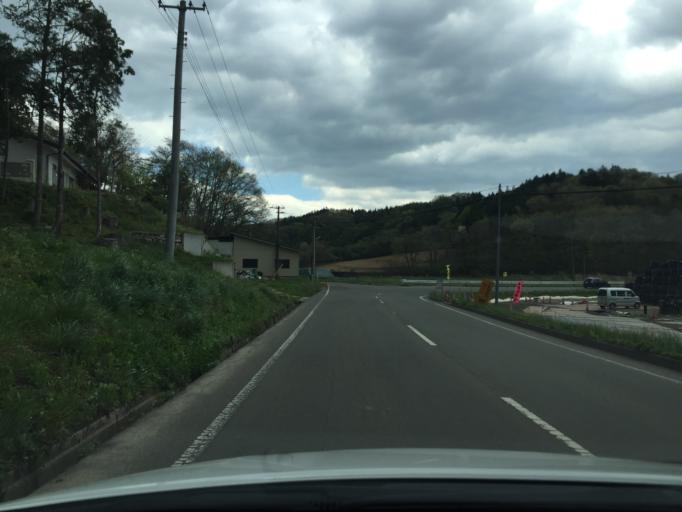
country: JP
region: Fukushima
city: Yanagawamachi-saiwaicho
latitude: 37.7077
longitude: 140.7473
